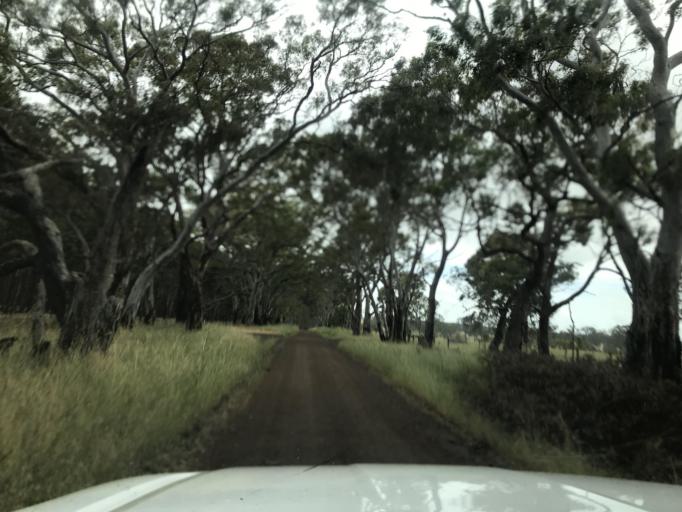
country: AU
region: South Australia
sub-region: Wattle Range
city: Penola
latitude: -37.2346
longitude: 141.4422
